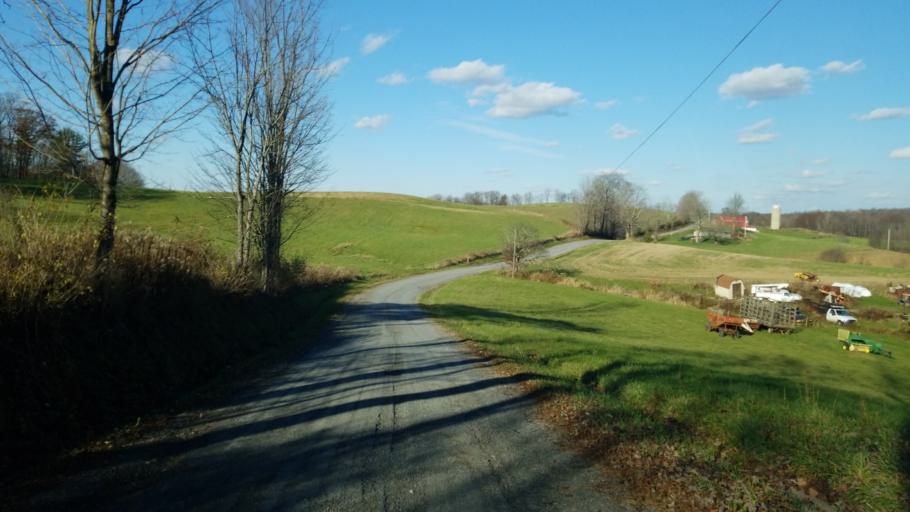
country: US
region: Pennsylvania
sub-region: Clearfield County
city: Treasure Lake
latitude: 41.1554
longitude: -78.6607
